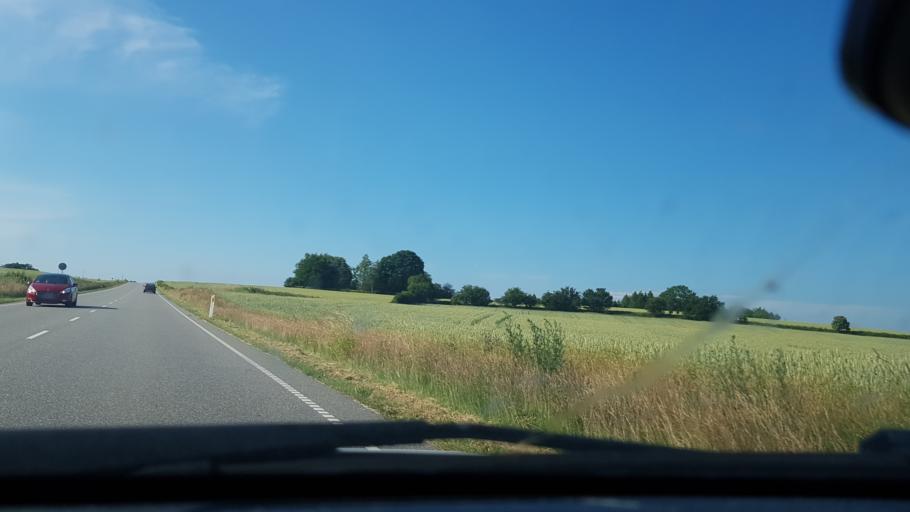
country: DK
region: Zealand
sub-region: Odsherred Kommune
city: Hojby
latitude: 55.8528
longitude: 11.5935
